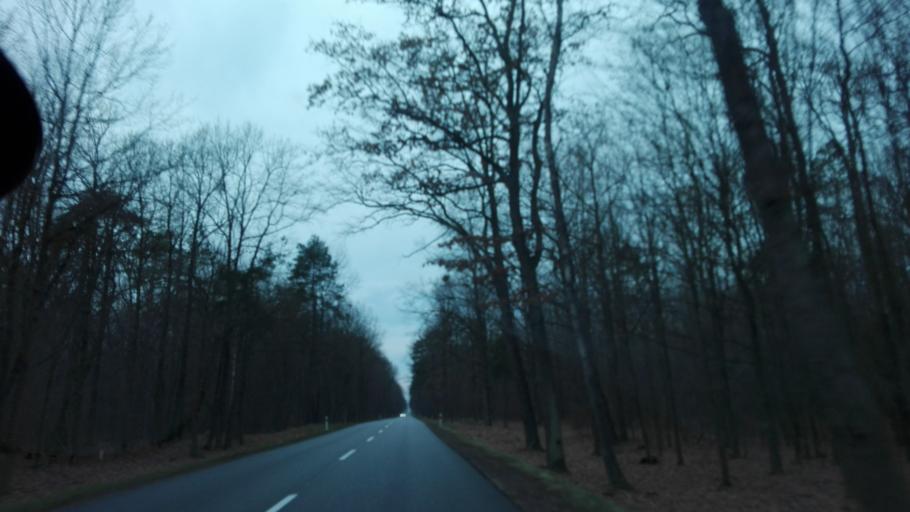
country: PL
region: Lublin Voivodeship
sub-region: Powiat radzynski
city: Wohyn
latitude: 51.7779
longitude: 22.8505
